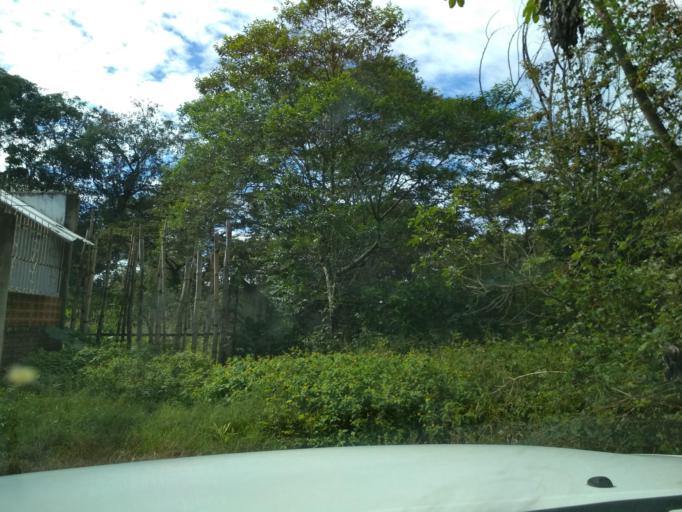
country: MX
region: Veracruz
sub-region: Coatepec
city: Las Lomas
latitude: 19.4362
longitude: -96.9228
